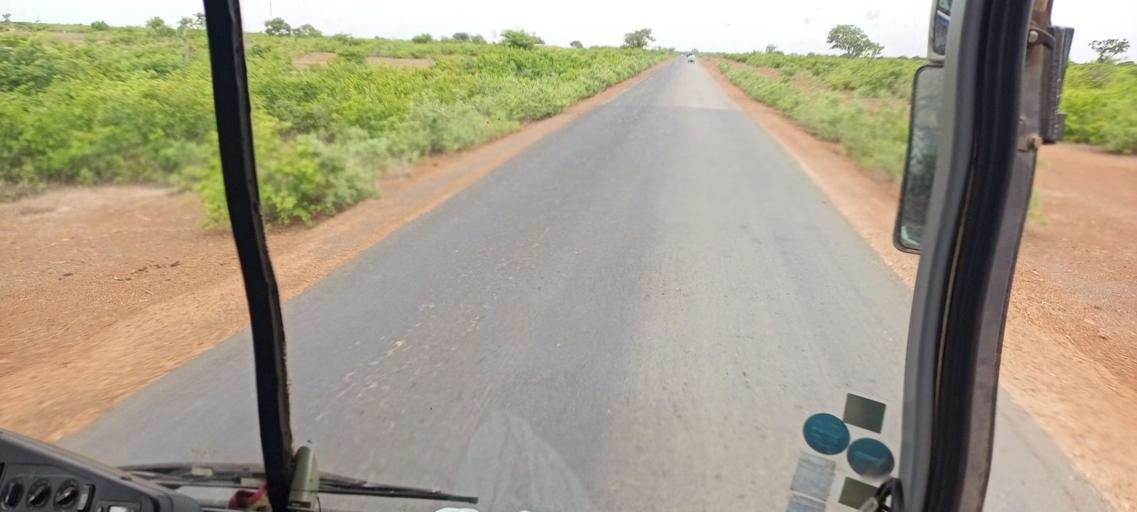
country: ML
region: Segou
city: Bla
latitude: 12.7587
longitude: -5.7371
